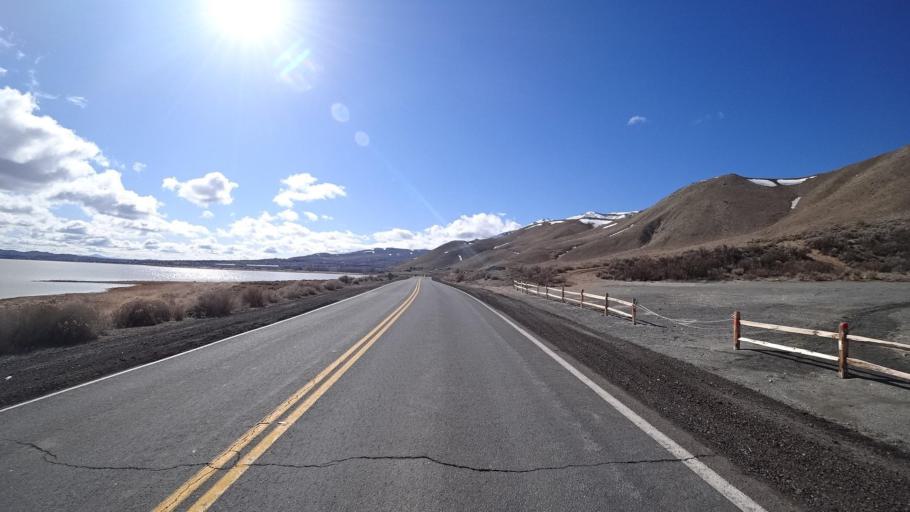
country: US
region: Nevada
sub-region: Washoe County
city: Cold Springs
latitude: 39.6474
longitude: -119.9272
